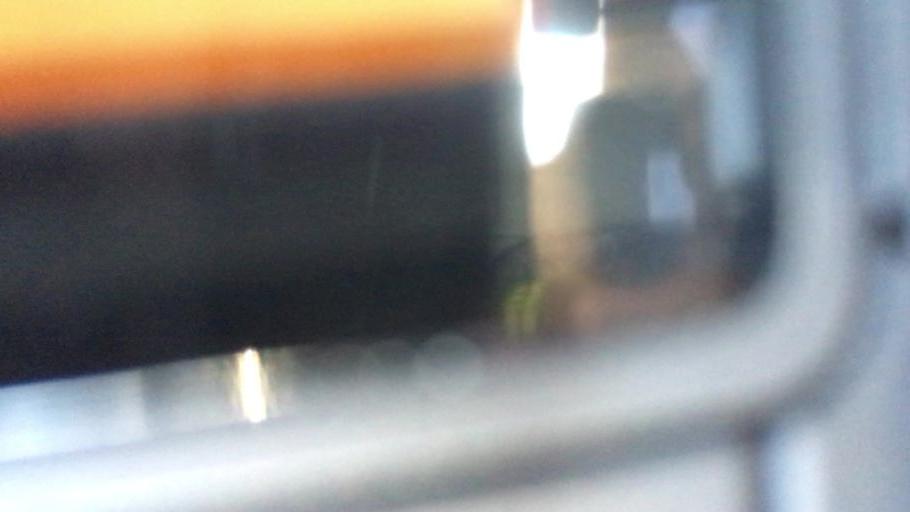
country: US
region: Maryland
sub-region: Wicomico County
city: Fruitland
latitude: 38.3110
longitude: -75.6280
